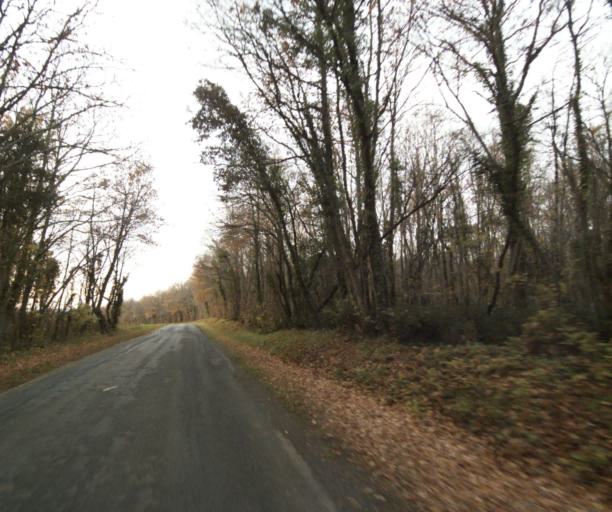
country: FR
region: Poitou-Charentes
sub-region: Departement de la Charente-Maritime
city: Bussac-sur-Charente
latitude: 45.8137
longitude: -0.6073
